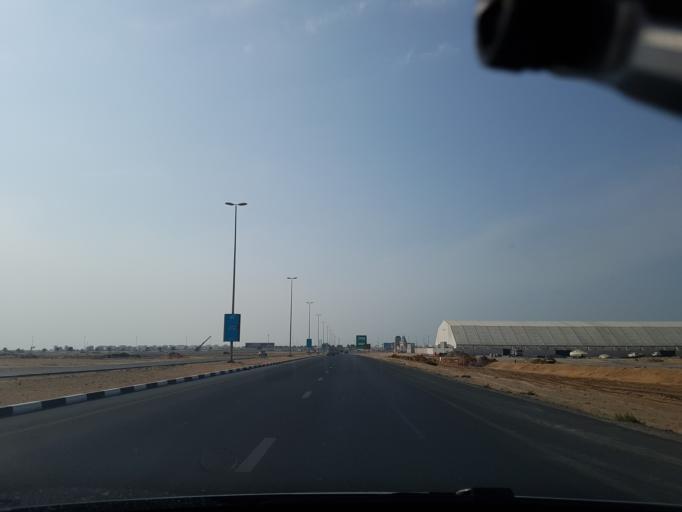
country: AE
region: Ajman
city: Ajman
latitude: 25.4322
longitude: 55.5096
